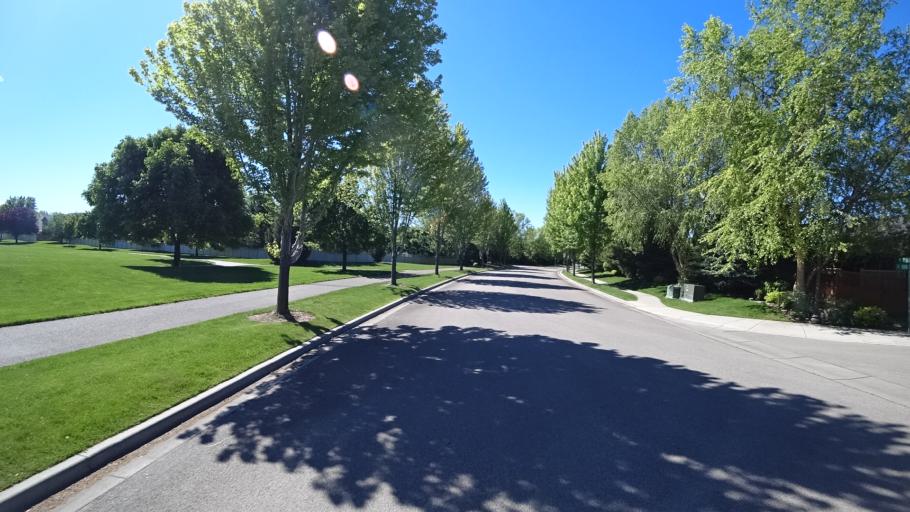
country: US
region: Idaho
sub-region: Ada County
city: Meridian
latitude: 43.6358
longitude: -116.3641
